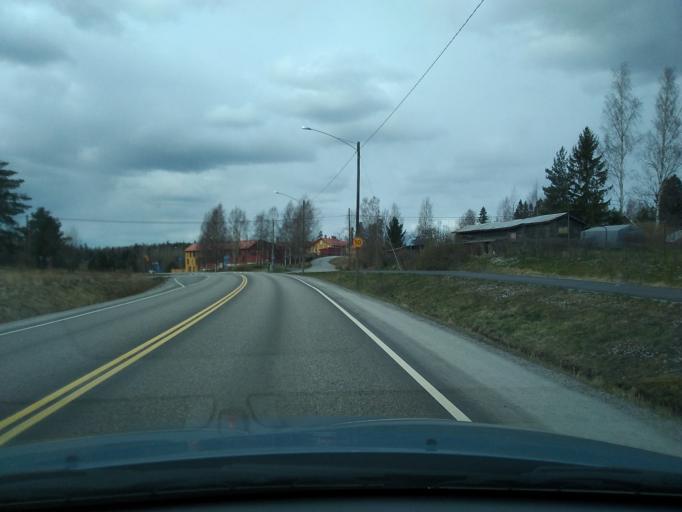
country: FI
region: Uusimaa
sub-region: Helsinki
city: Pornainen
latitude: 60.3375
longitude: 25.4800
